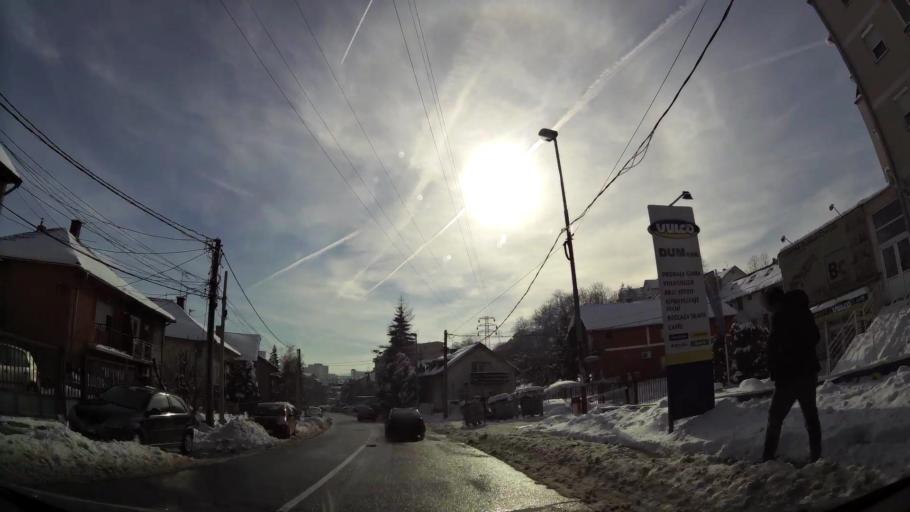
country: RS
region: Central Serbia
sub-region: Belgrade
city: Palilula
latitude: 44.7962
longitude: 20.5222
